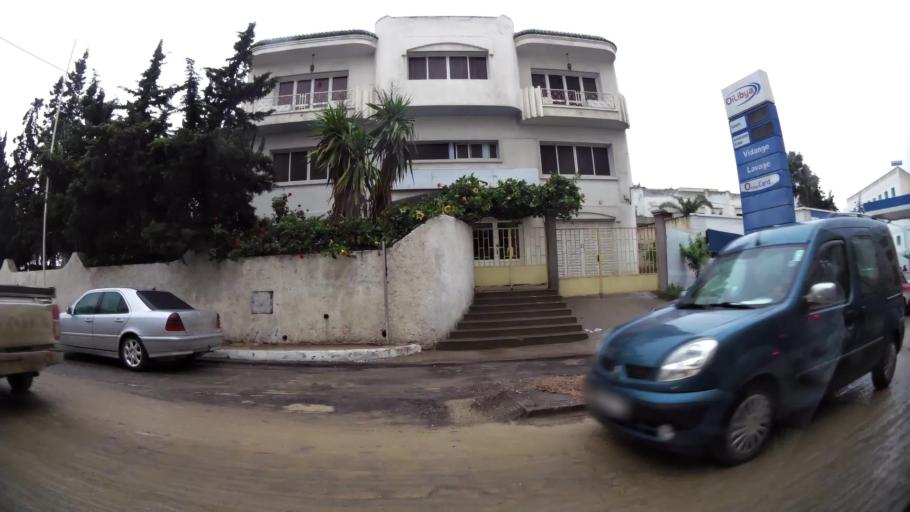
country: MA
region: Taza-Al Hoceima-Taounate
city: Al Hoceima
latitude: 35.2399
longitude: -3.9280
